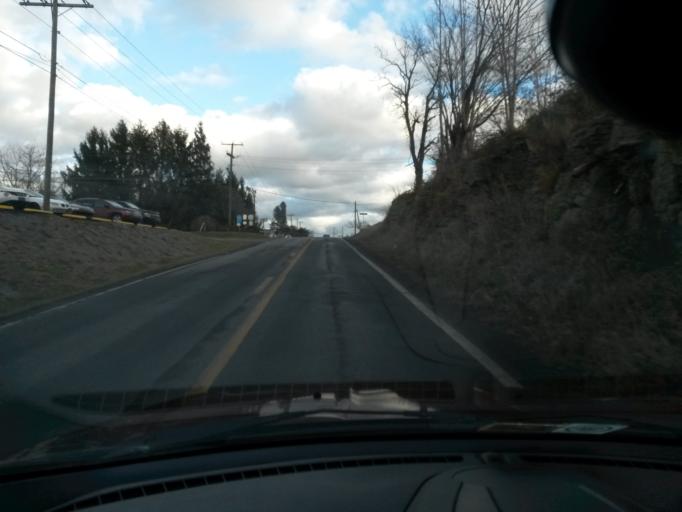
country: US
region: West Virginia
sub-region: Monroe County
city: Union
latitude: 37.5908
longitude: -80.5345
